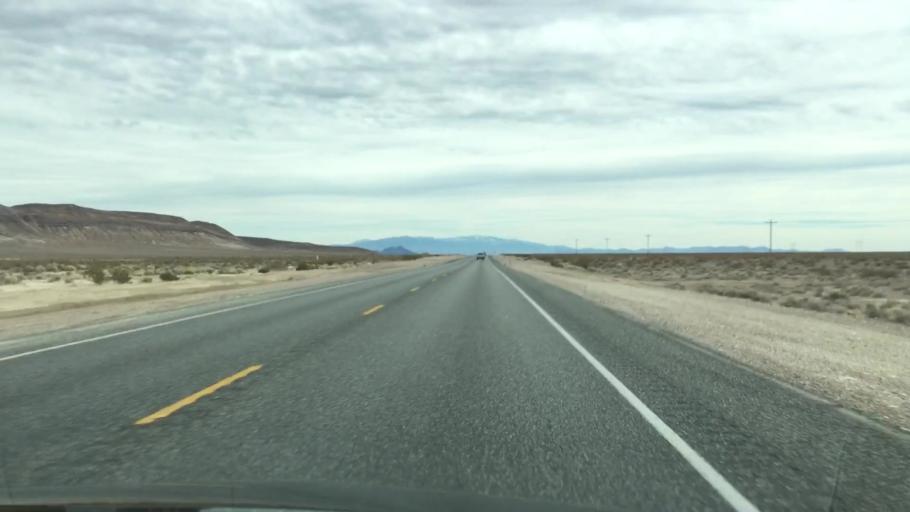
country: US
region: Nevada
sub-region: Nye County
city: Beatty
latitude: 36.6951
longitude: -116.5725
